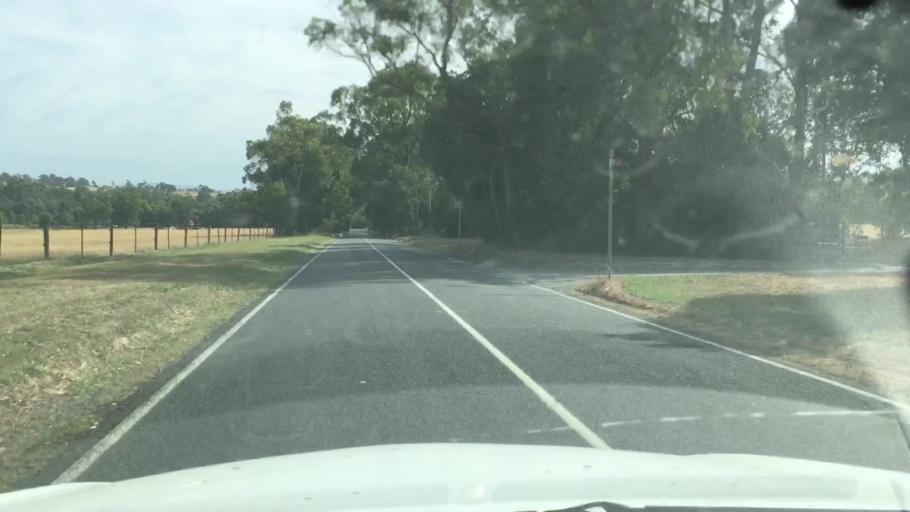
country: AU
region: Victoria
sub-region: Yarra Ranges
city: Woori Yallock
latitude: -37.8221
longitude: 145.4952
